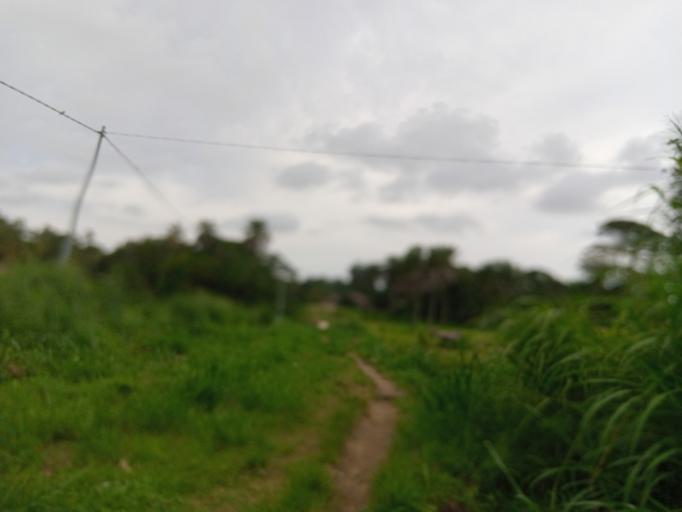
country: SL
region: Northern Province
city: Masoyila
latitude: 8.5973
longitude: -13.2017
